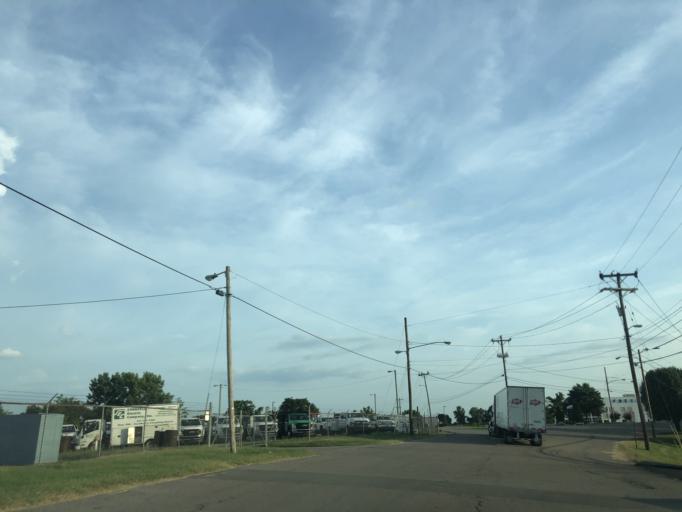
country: US
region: Tennessee
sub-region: Davidson County
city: Nashville
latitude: 36.1537
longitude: -86.7131
